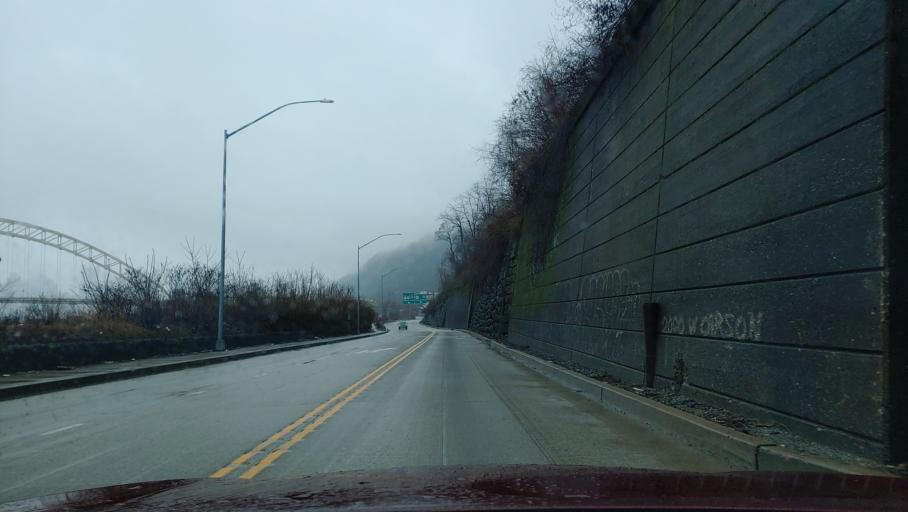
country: US
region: Pennsylvania
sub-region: Allegheny County
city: Ingram
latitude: 40.4474
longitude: -80.0326
